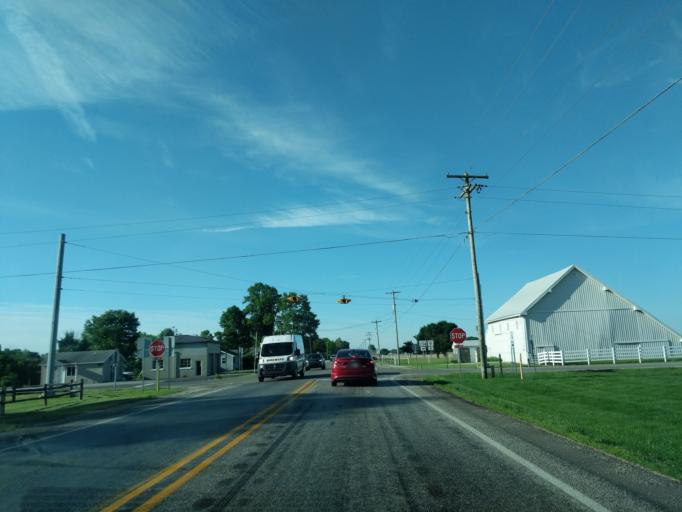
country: US
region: Indiana
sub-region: Madison County
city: Ingalls
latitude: 39.9015
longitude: -85.7707
